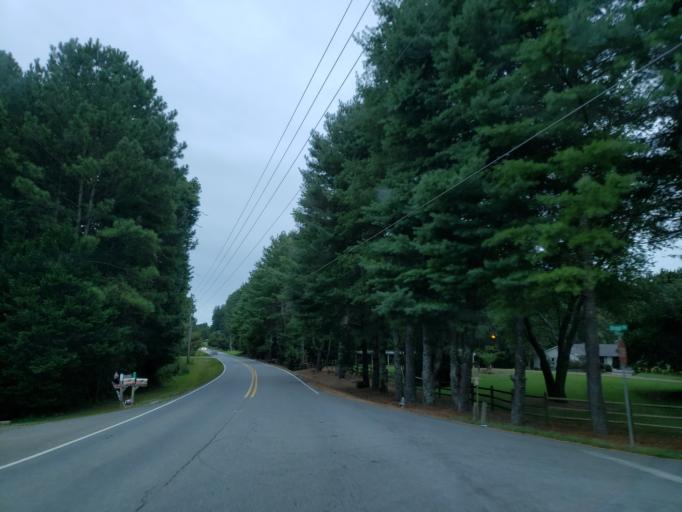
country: US
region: Georgia
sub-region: Cherokee County
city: Canton
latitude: 34.3446
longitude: -84.4919
